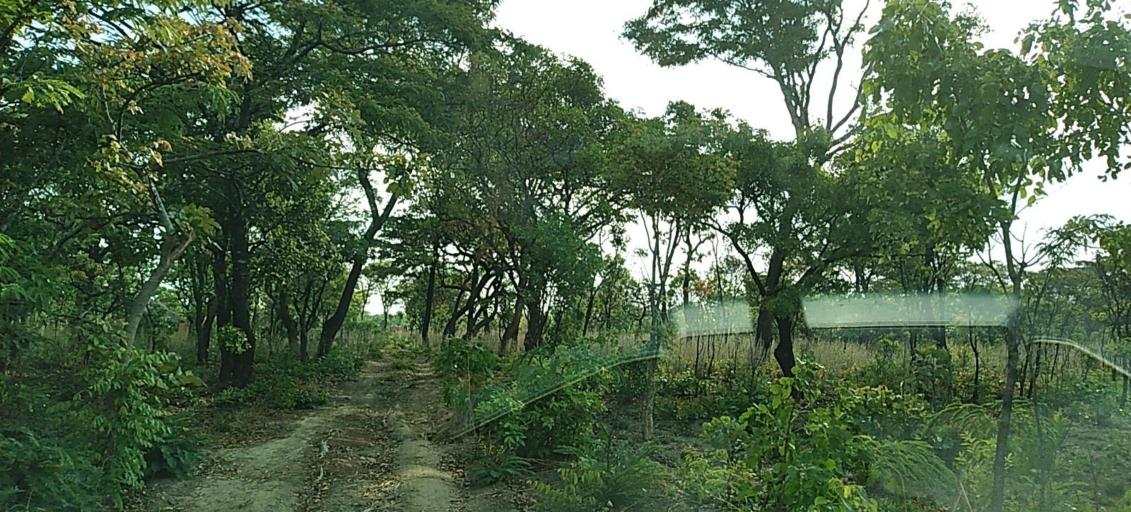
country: ZM
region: Copperbelt
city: Chililabombwe
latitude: -12.3604
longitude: 27.3921
